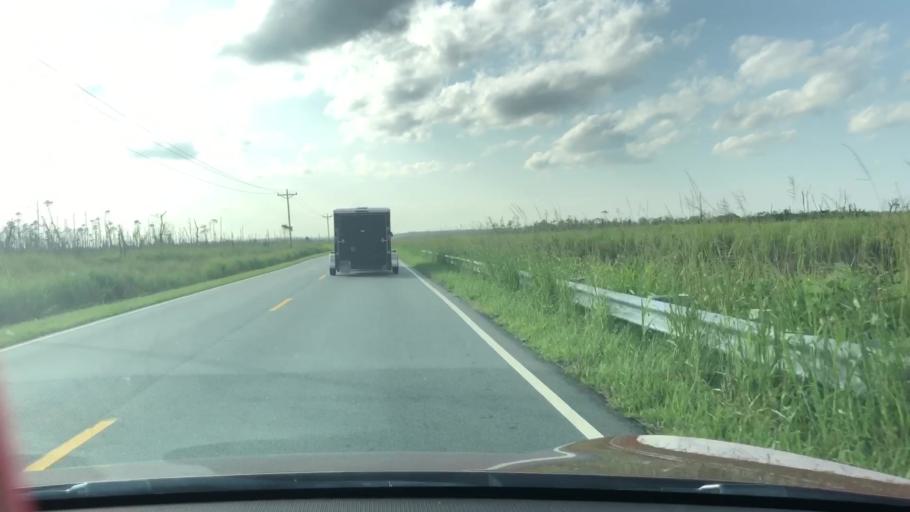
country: US
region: North Carolina
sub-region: Dare County
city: Wanchese
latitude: 35.6247
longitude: -75.8447
